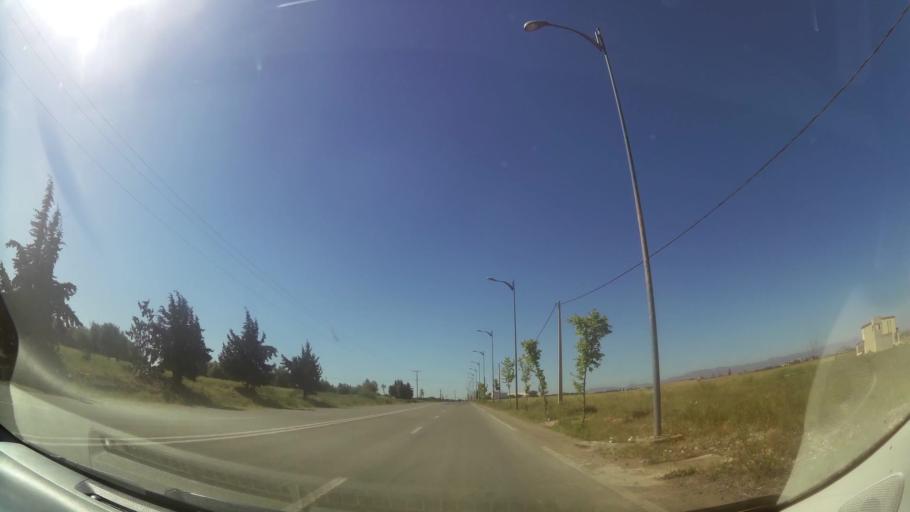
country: MA
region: Oriental
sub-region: Oujda-Angad
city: Oujda
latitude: 34.7232
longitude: -1.8669
